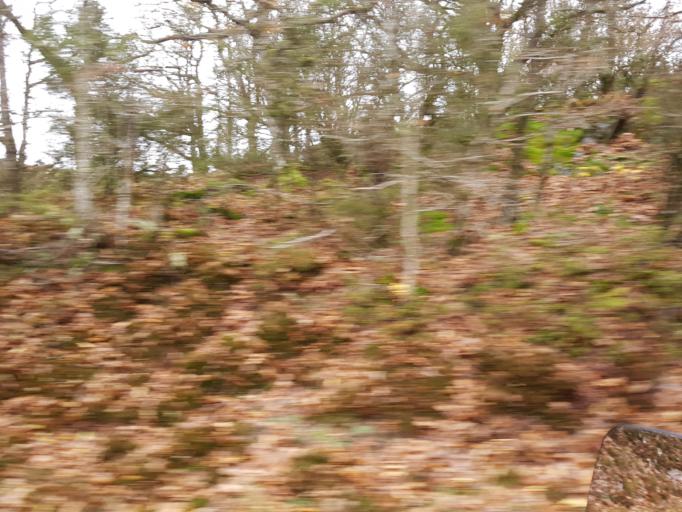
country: SE
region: Vaestra Goetaland
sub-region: Orust
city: Henan
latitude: 58.1665
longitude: 11.7242
